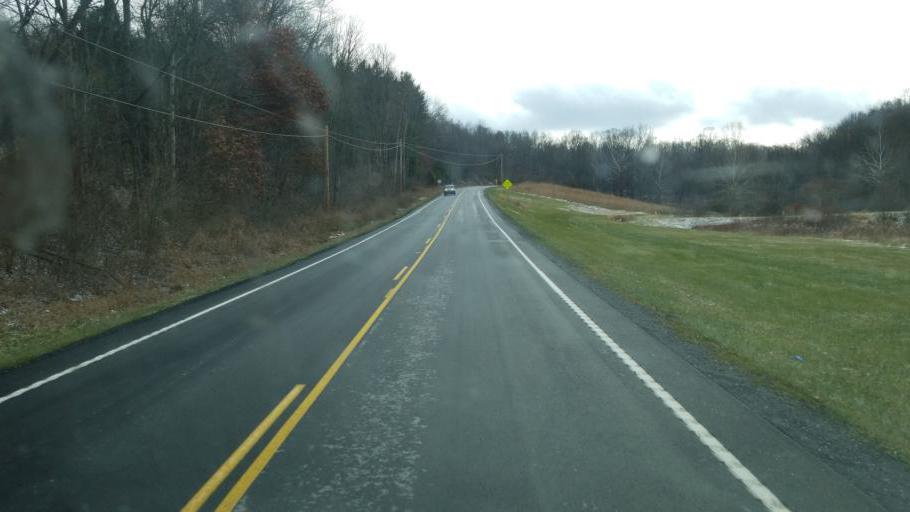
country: US
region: Ohio
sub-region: Muskingum County
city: Frazeysburg
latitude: 40.1202
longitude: -82.1875
